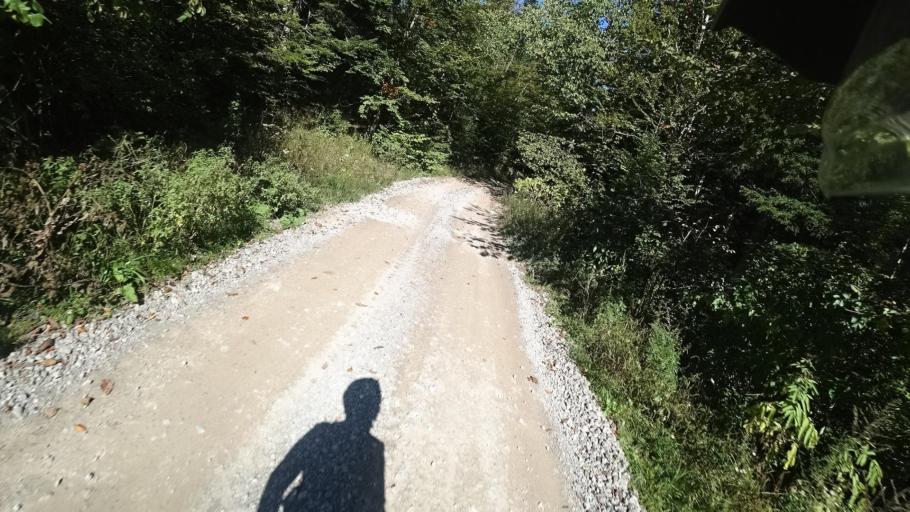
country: HR
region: Karlovacka
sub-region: Grad Ogulin
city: Ogulin
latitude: 45.2176
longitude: 15.1506
